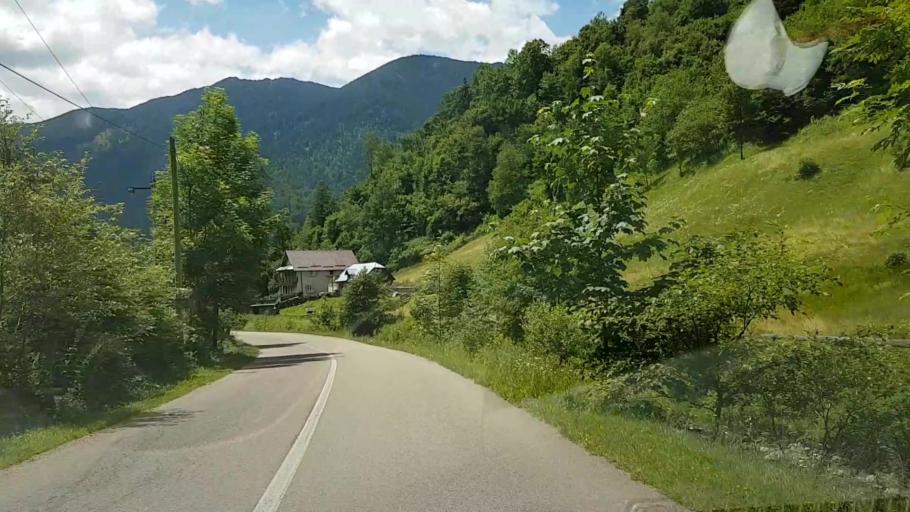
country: RO
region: Suceava
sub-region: Comuna Crucea
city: Crucea
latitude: 47.4060
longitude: 25.5753
